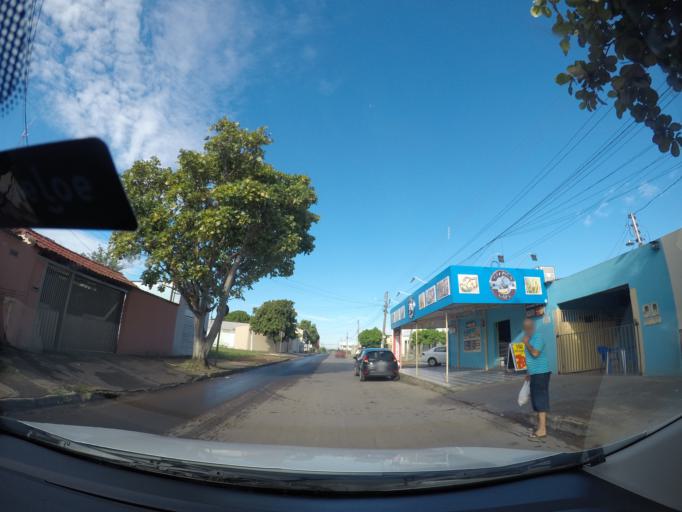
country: BR
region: Goias
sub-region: Aparecida De Goiania
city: Aparecida de Goiania
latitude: -16.7546
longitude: -49.2769
